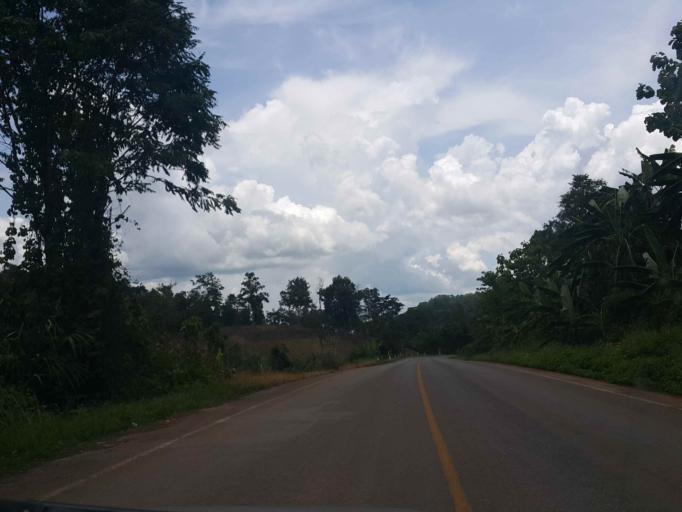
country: TH
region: Phayao
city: Chiang Muan
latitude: 18.9055
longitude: 100.1210
